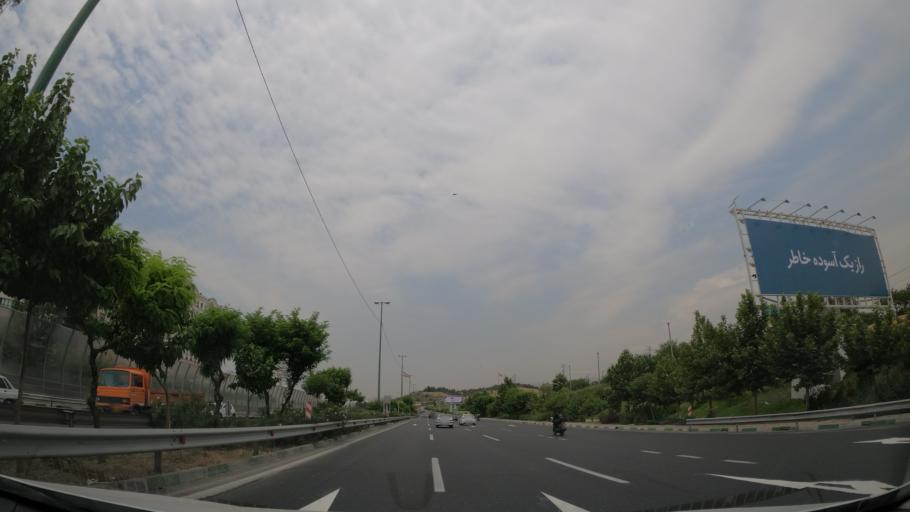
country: IR
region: Tehran
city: Tehran
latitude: 35.7403
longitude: 51.3519
